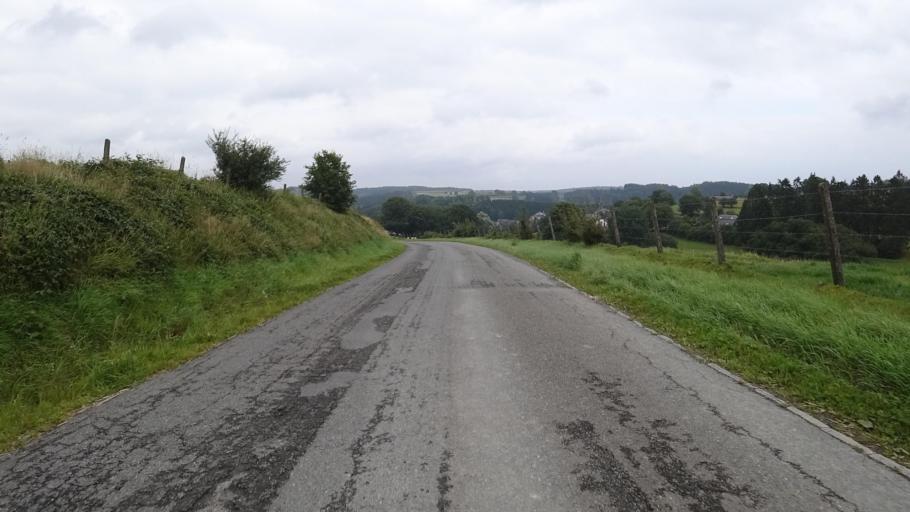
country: BE
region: Wallonia
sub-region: Province du Luxembourg
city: Chiny
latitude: 49.8056
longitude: 5.3528
